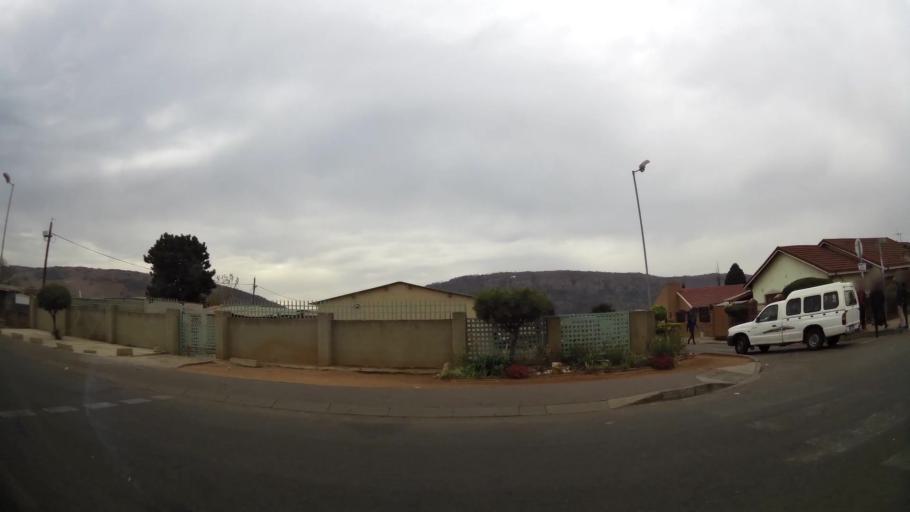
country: ZA
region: Gauteng
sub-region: City of Tshwane Metropolitan Municipality
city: Cullinan
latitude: -25.7095
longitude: 28.3589
